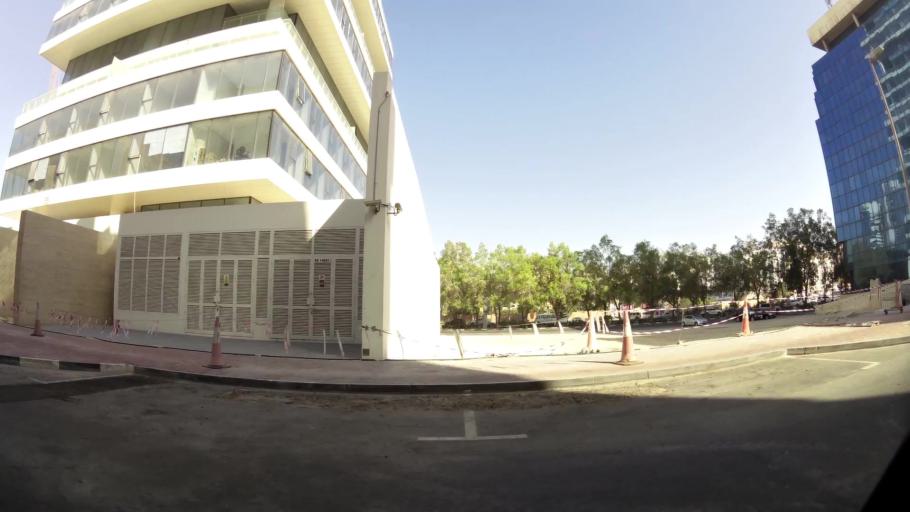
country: AE
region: Ash Shariqah
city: Sharjah
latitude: 25.2529
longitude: 55.2928
